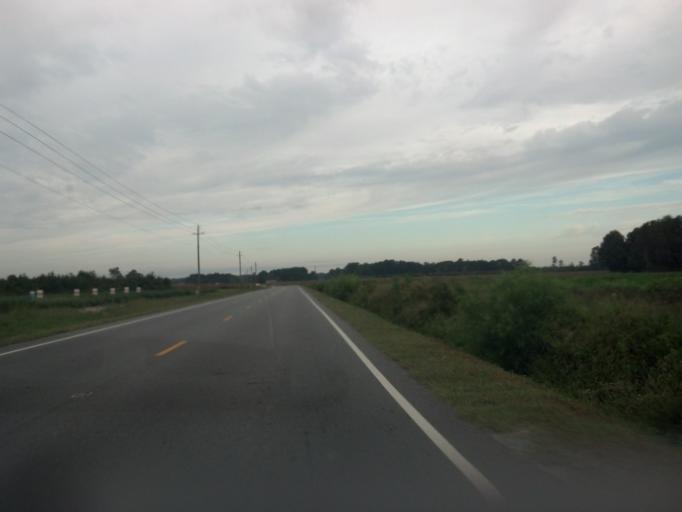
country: US
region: North Carolina
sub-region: Pitt County
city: Ayden
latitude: 35.4765
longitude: -77.4454
